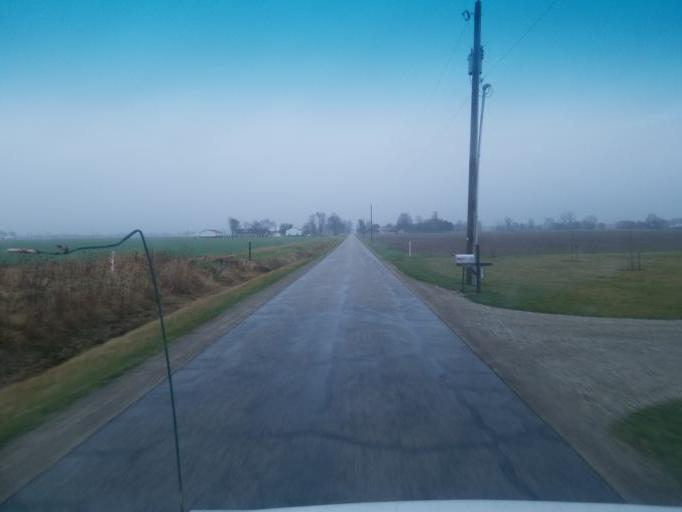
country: US
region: Ohio
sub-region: Henry County
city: Napoleon
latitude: 41.4133
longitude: -84.2142
